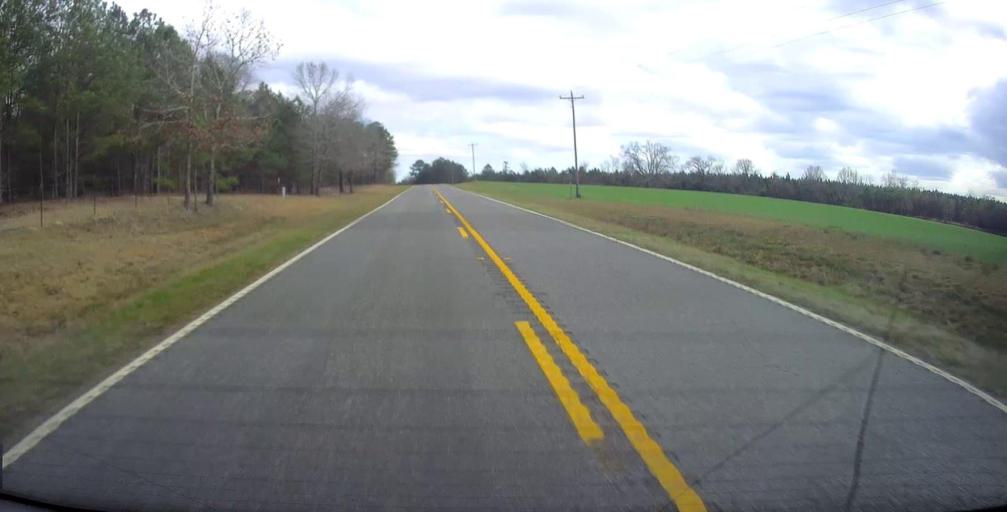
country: US
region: Georgia
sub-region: Marion County
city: Buena Vista
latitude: 32.4380
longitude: -84.4347
